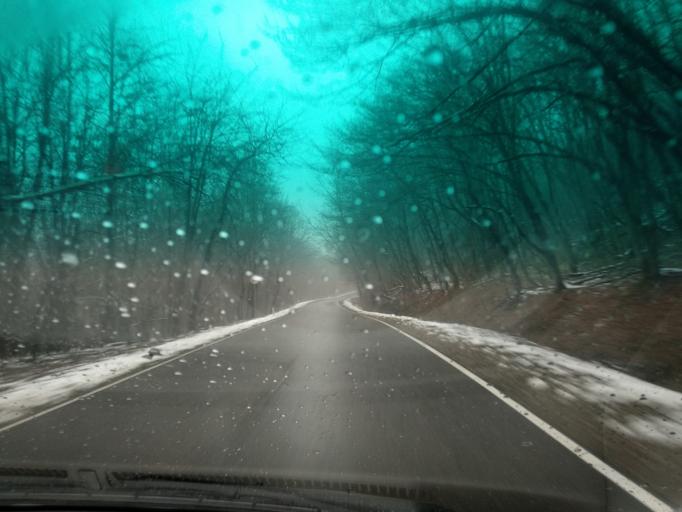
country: RU
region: Krasnodarskiy
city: Khadyzhensk
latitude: 44.2646
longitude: 39.3600
